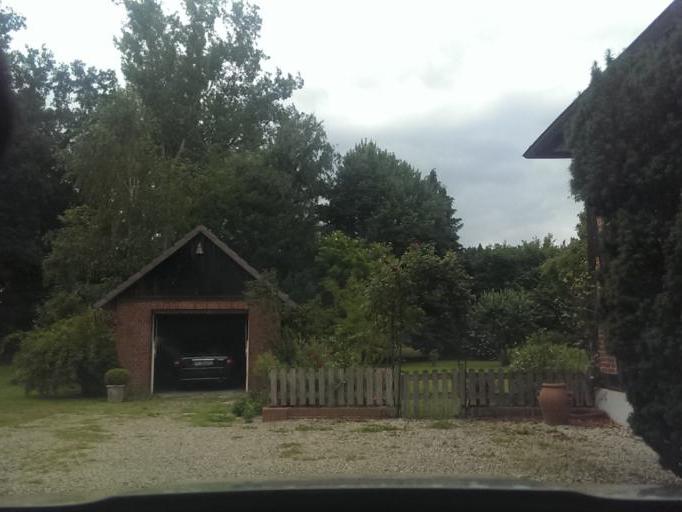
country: DE
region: North Rhine-Westphalia
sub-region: Regierungsbezirk Detmold
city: Delbruck
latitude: 51.7606
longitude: 8.5494
